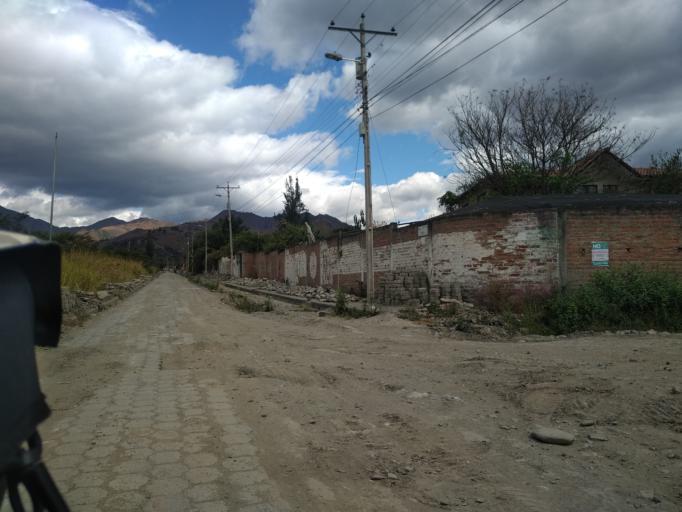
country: EC
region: Loja
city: Loja
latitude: -4.2539
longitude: -79.2236
